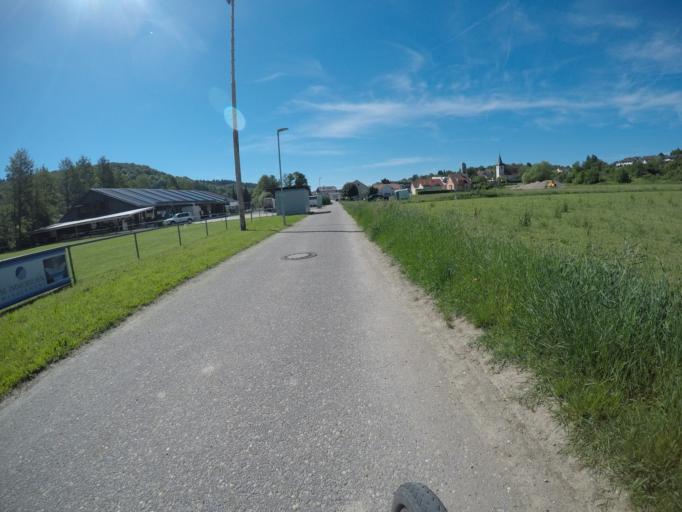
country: DE
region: Baden-Wuerttemberg
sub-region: Karlsruhe Region
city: Konigsbach-Stein
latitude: 48.9539
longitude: 8.6207
